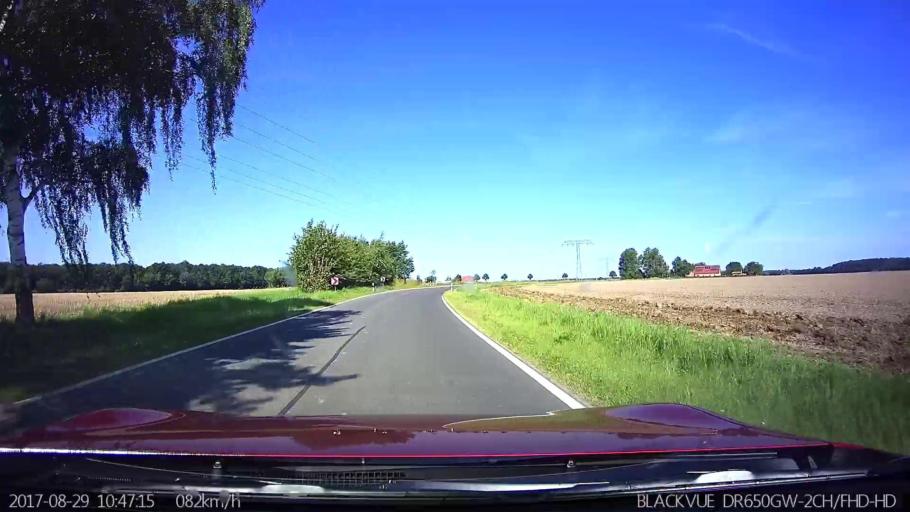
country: DE
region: Mecklenburg-Vorpommern
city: Velgast
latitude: 54.2251
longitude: 12.8313
